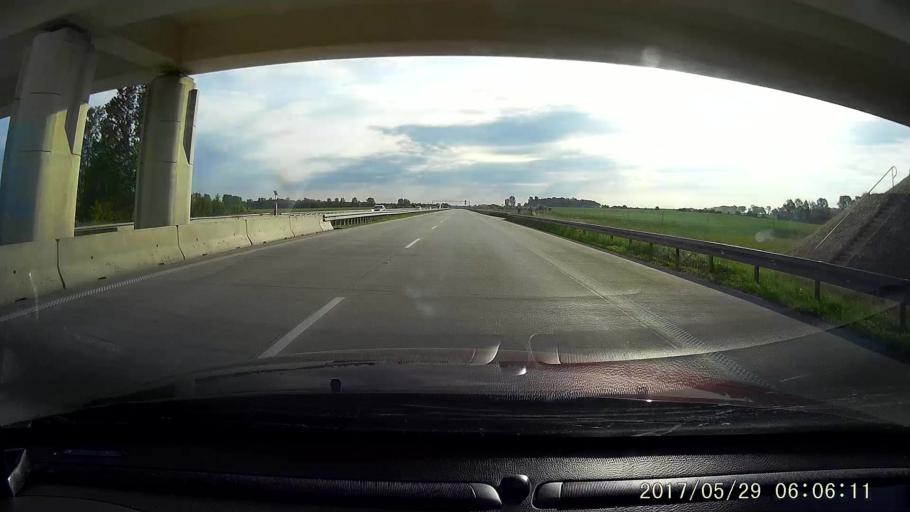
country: PL
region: Lower Silesian Voivodeship
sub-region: Powiat zgorzelecki
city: Lagow
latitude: 51.1805
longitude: 15.0919
